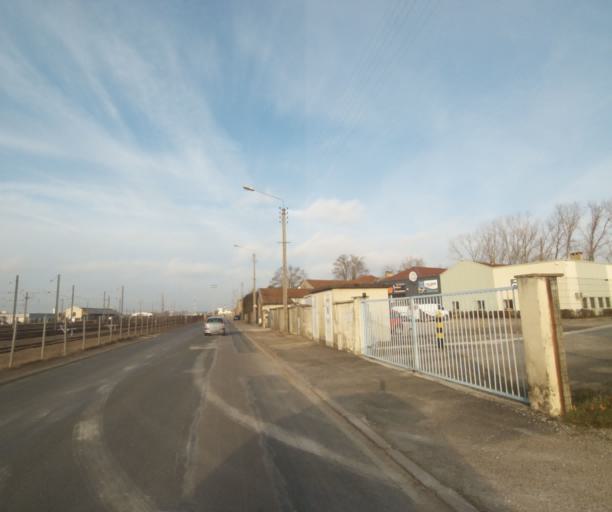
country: FR
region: Champagne-Ardenne
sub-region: Departement de la Haute-Marne
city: Saint-Dizier
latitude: 48.6432
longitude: 4.9485
